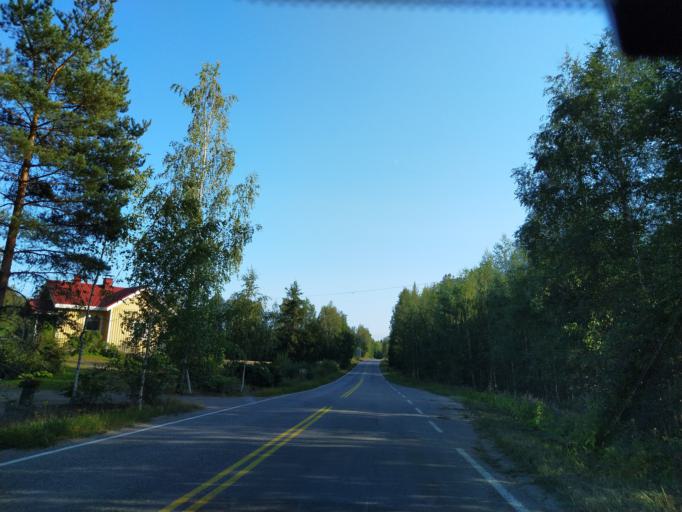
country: FI
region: Central Finland
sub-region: Jaemsae
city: Kuhmoinen
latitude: 61.5977
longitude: 25.1682
